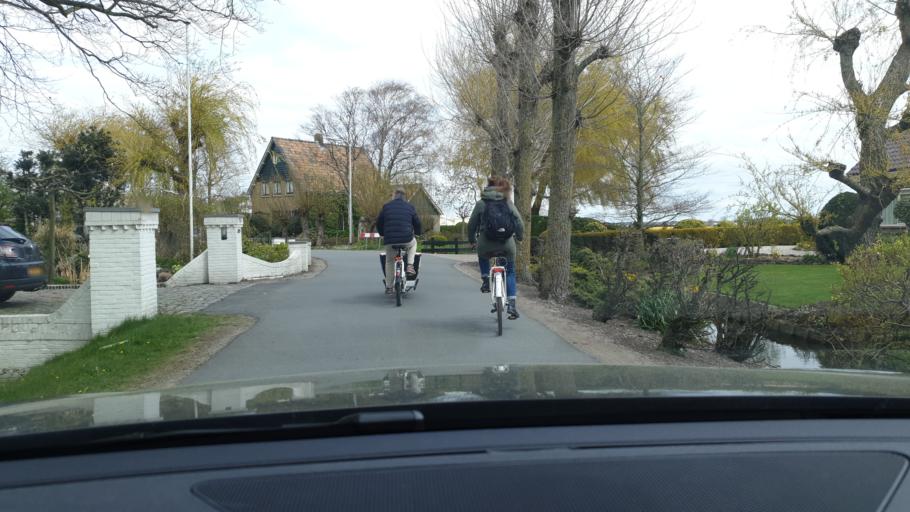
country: NL
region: South Holland
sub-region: Gemeente Lisse
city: Lisse
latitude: 52.2905
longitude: 4.5352
